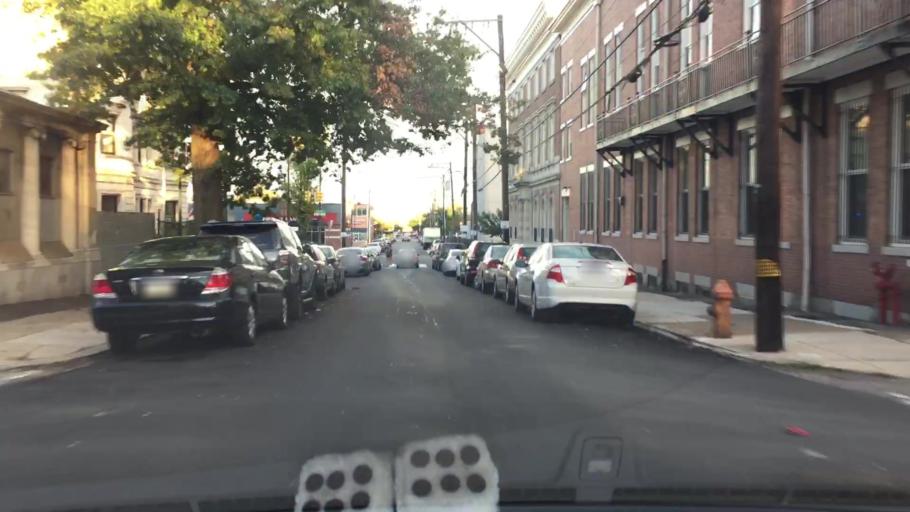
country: US
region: Pennsylvania
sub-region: Philadelphia County
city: Philadelphia
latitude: 39.9760
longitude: -75.1595
